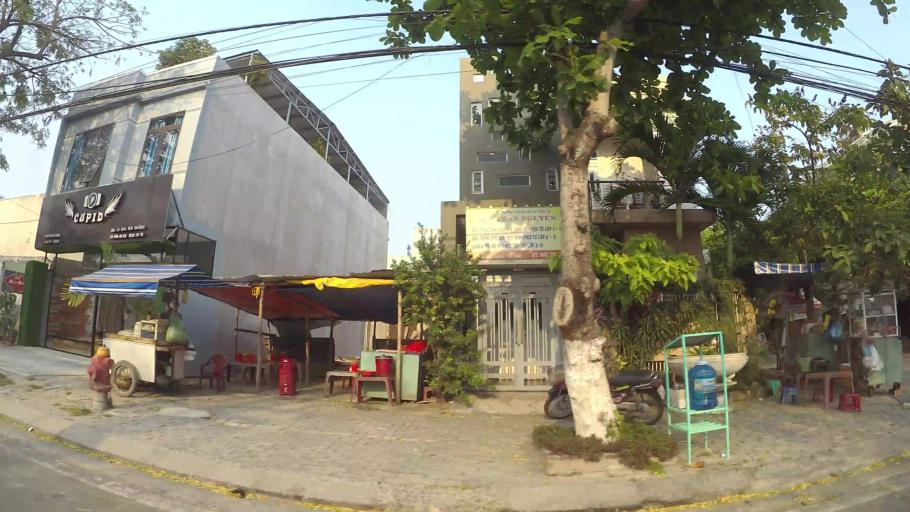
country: VN
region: Da Nang
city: Cam Le
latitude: 16.0223
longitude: 108.2024
